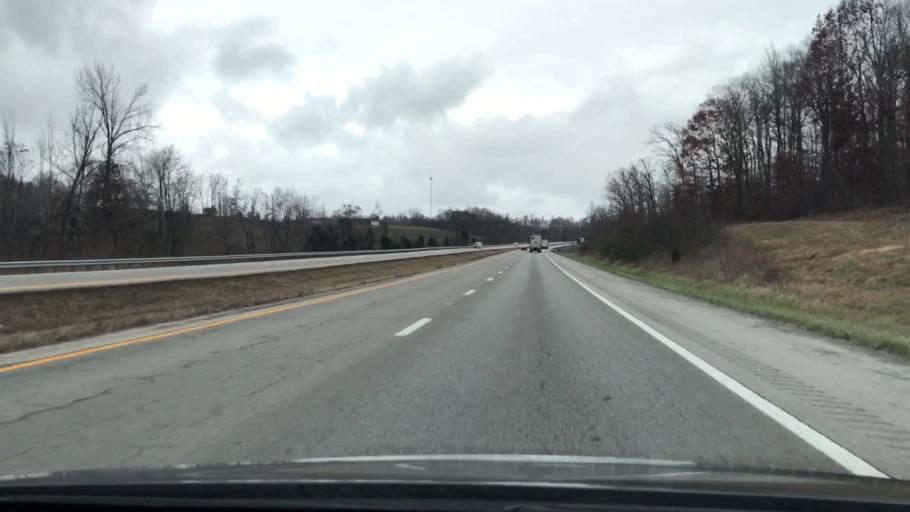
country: US
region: Kentucky
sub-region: Christian County
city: Hopkinsville
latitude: 36.9137
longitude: -87.4740
